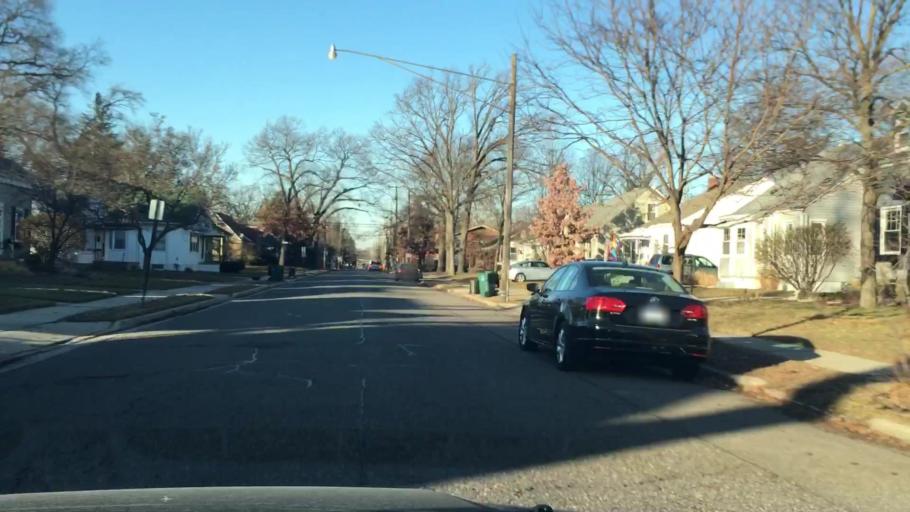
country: US
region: Michigan
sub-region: Oakland County
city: Ferndale
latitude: 42.4531
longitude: -83.1377
